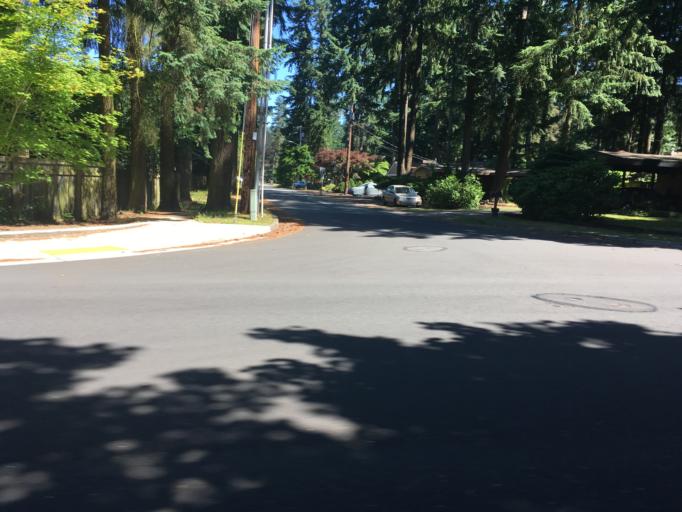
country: US
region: Washington
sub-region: King County
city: Redmond
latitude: 47.6315
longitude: -122.1288
